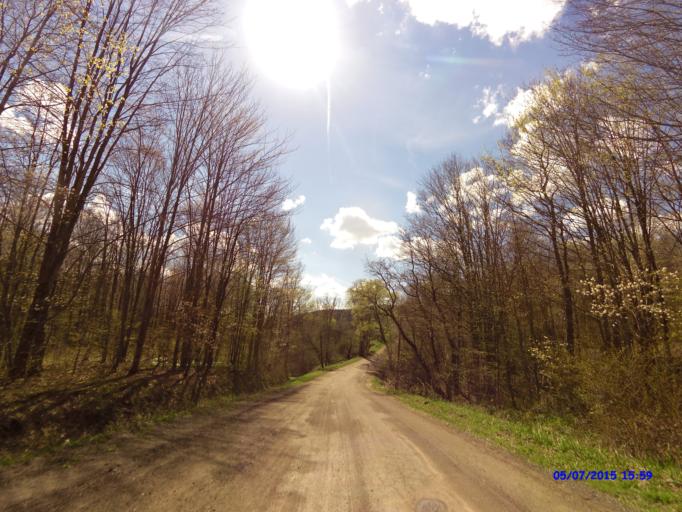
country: US
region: New York
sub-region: Cattaraugus County
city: Franklinville
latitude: 42.2981
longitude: -78.5915
